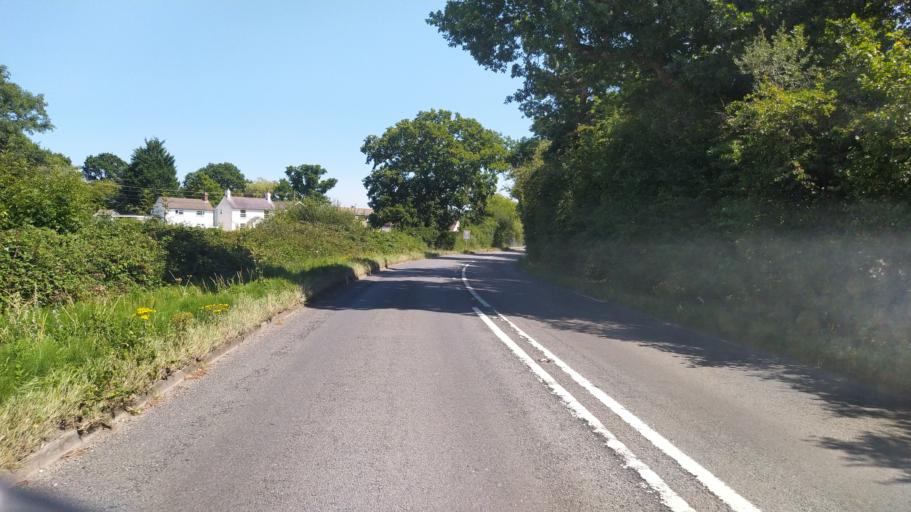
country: GB
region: England
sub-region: Hampshire
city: Cadnam
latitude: 50.9165
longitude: -1.5383
